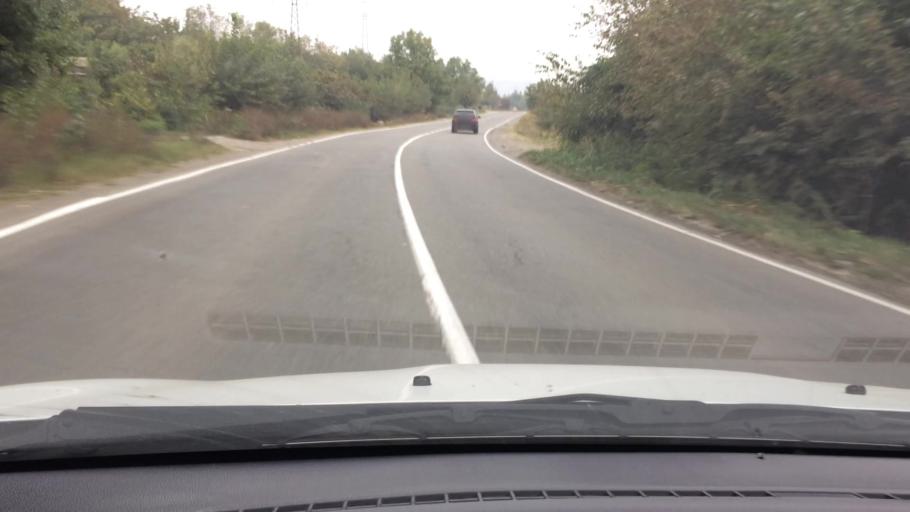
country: GE
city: Naghvarevi
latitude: 41.2982
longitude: 44.7889
